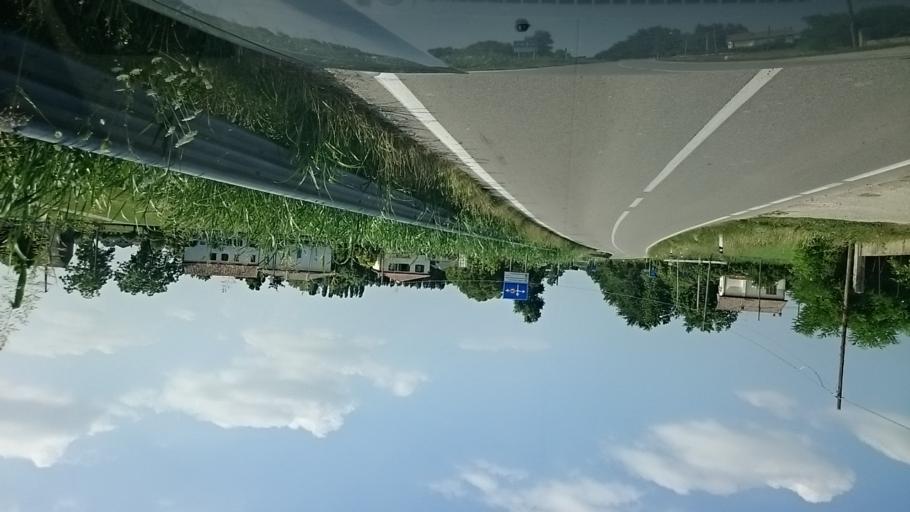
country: IT
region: Veneto
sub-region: Provincia di Padova
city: Villa del Conte
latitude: 45.5646
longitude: 11.8662
